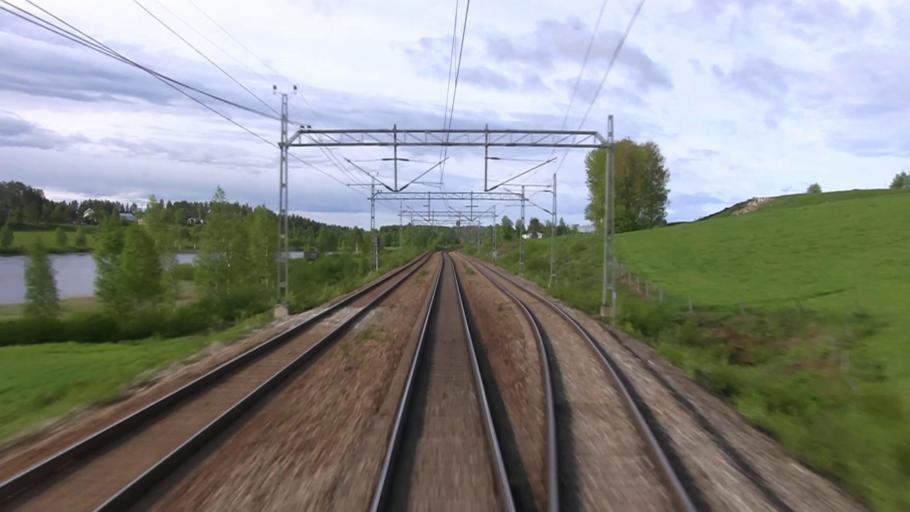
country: SE
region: Vaesterbotten
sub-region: Vindelns Kommun
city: Vindeln
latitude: 64.1023
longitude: 19.6805
